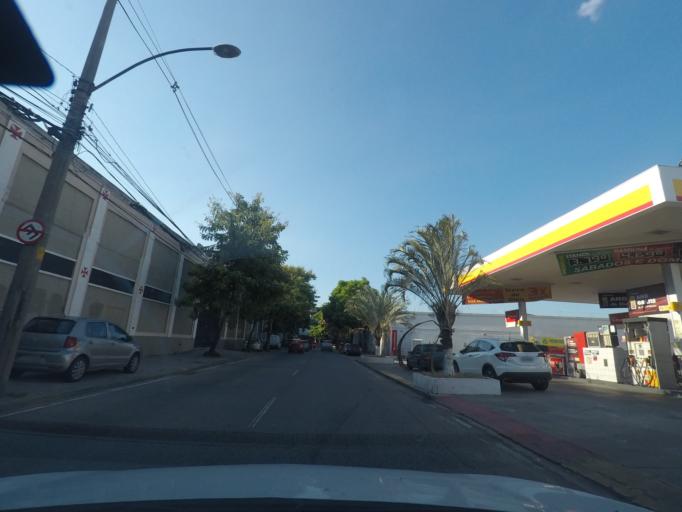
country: BR
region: Rio de Janeiro
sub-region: Rio De Janeiro
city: Rio de Janeiro
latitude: -22.8901
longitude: -43.2275
